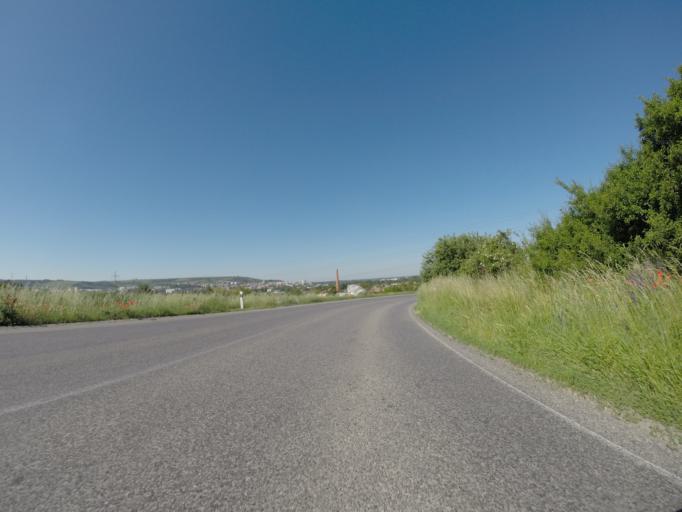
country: SK
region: Trnavsky
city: Hlohovec
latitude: 48.4453
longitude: 17.8150
